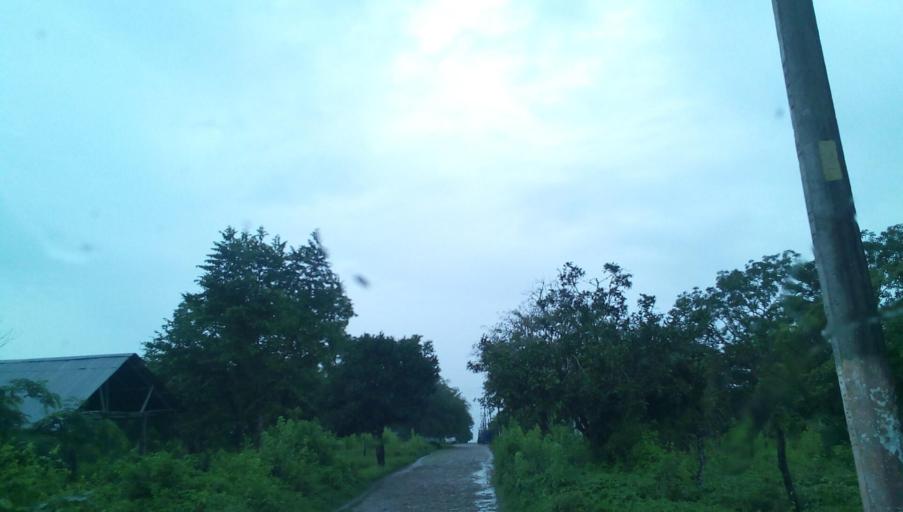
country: MX
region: Veracruz
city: Tempoal de Sanchez
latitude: 21.4190
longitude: -98.4280
